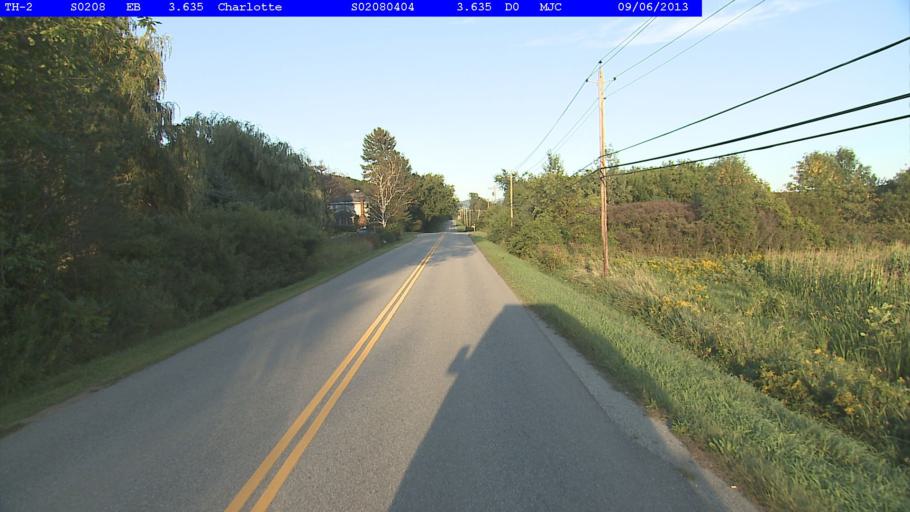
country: US
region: Vermont
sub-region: Chittenden County
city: Hinesburg
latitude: 44.3214
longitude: -73.1758
